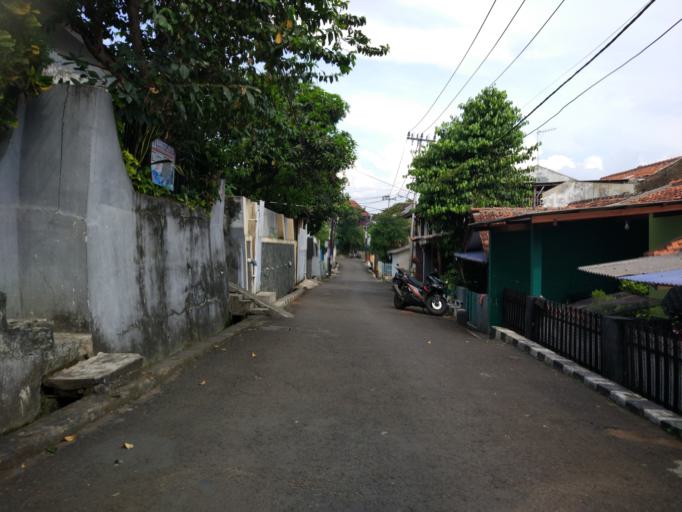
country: ID
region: West Java
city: Bandung
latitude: -6.9040
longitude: 107.6899
